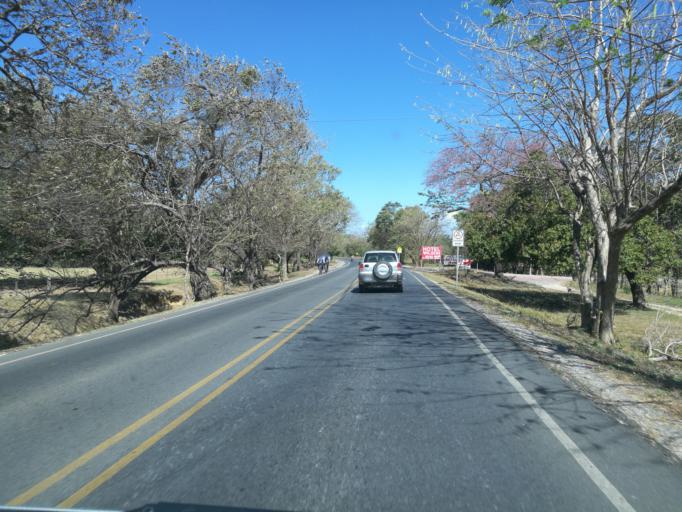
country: CR
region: Guanacaste
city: Liberia
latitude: 10.6428
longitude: -85.4541
